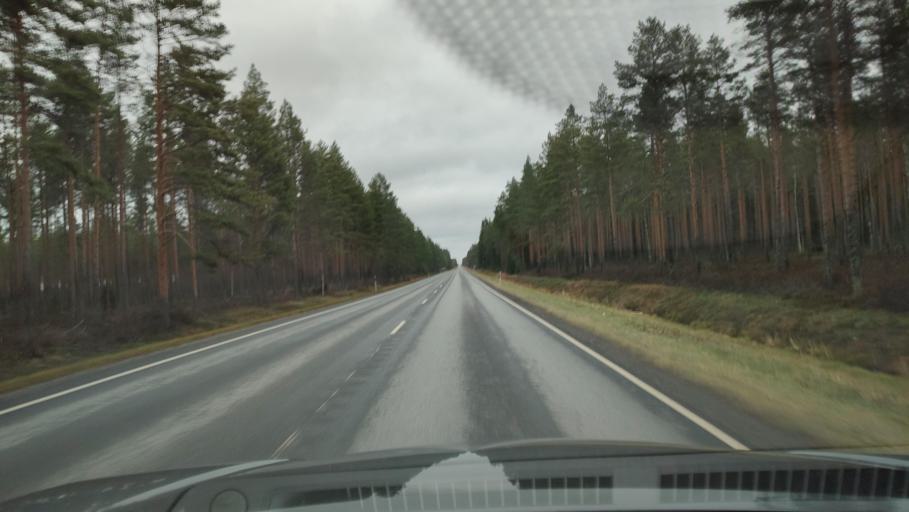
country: FI
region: Southern Ostrobothnia
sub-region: Seinaejoki
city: Kurikka
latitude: 62.5167
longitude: 22.3143
